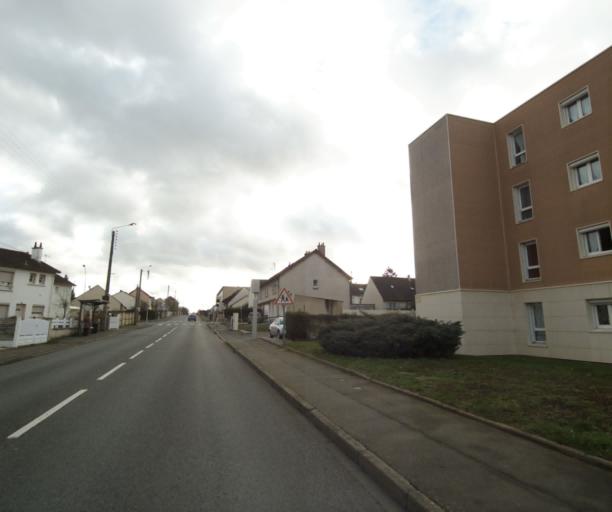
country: FR
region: Pays de la Loire
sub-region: Departement de la Sarthe
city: Le Mans
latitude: 47.9701
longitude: 0.2104
